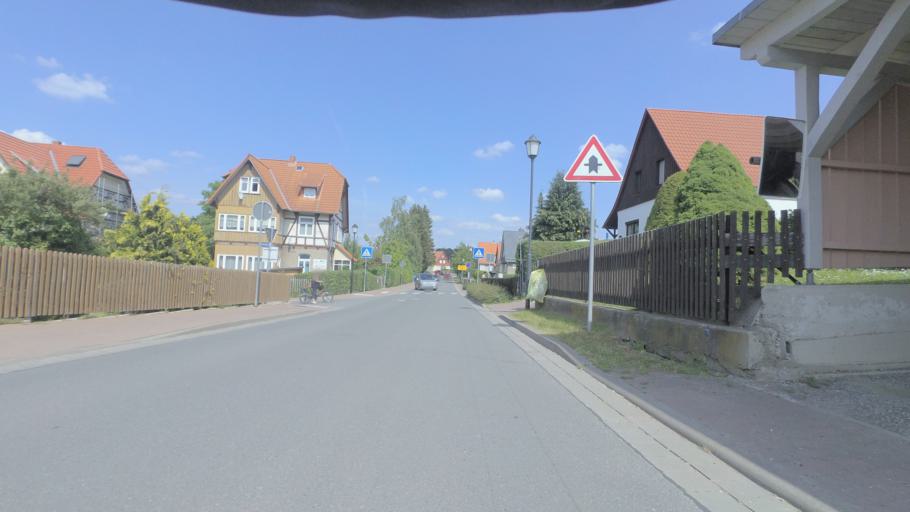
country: DE
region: Saxony-Anhalt
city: Ilsenburg
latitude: 51.8628
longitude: 10.6849
